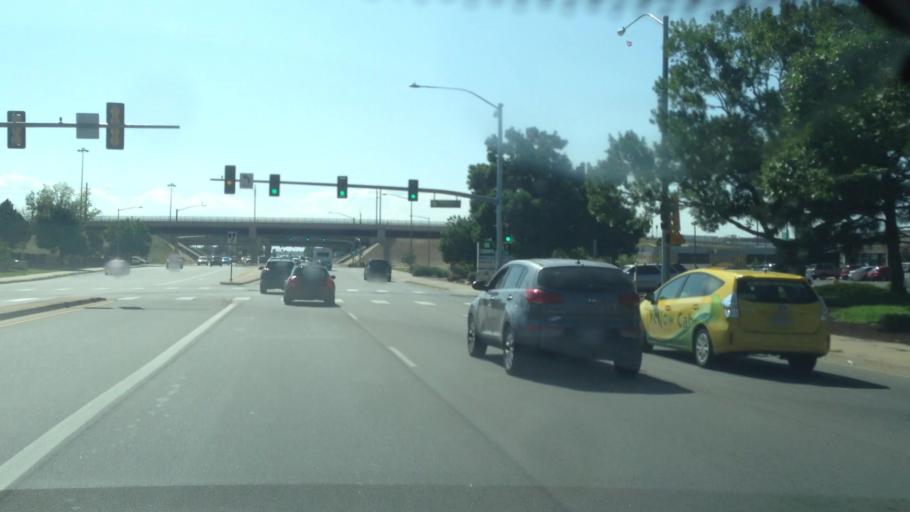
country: US
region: Colorado
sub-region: Adams County
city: Aurora
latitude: 39.7257
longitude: -104.8209
